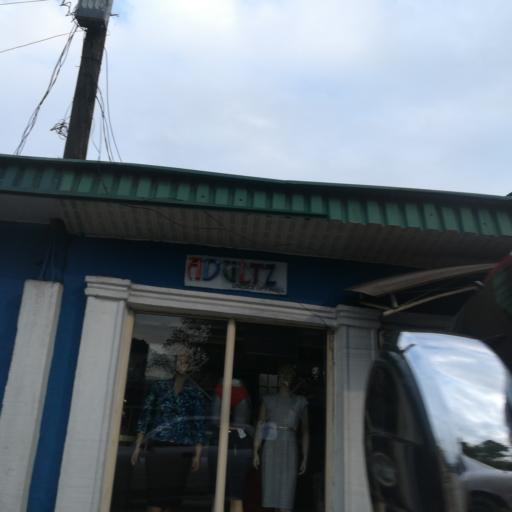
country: NG
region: Rivers
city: Port Harcourt
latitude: 4.8465
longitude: 7.0479
